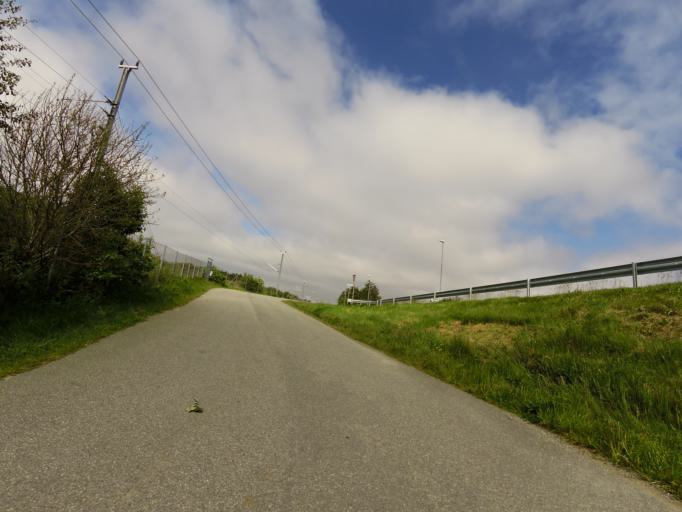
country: NO
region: Rogaland
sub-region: Ha
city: Vigrestad
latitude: 58.5214
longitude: 5.8003
